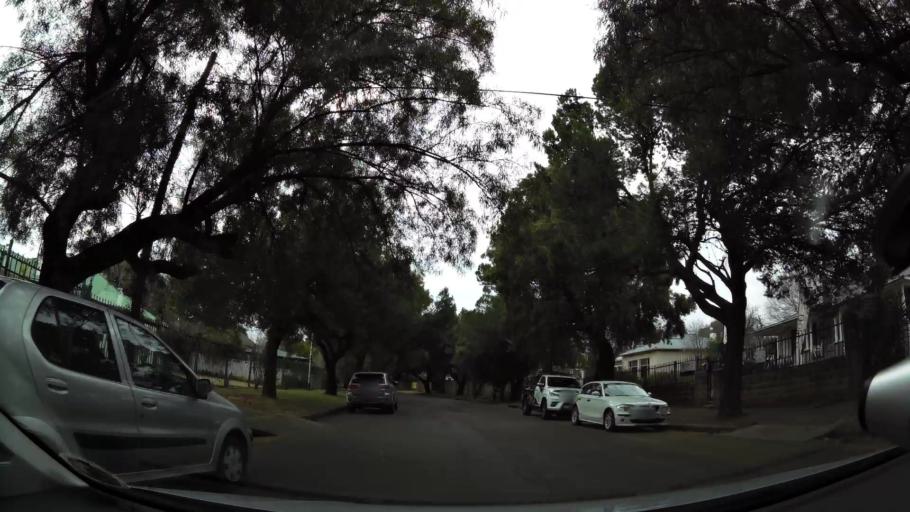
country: ZA
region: Orange Free State
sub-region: Mangaung Metropolitan Municipality
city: Bloemfontein
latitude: -29.1035
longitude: 26.2093
